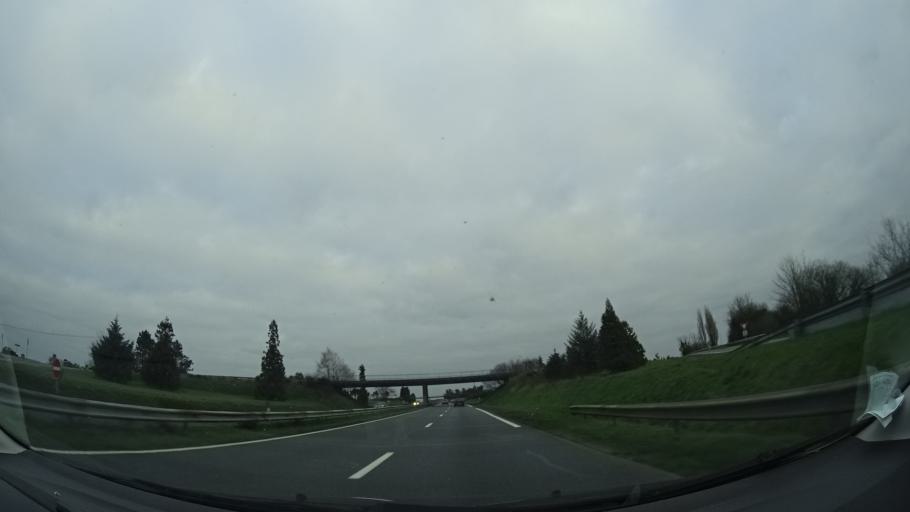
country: FR
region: Brittany
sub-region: Departement du Finistere
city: Saint-Thegonnec
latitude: 48.5280
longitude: -3.9423
